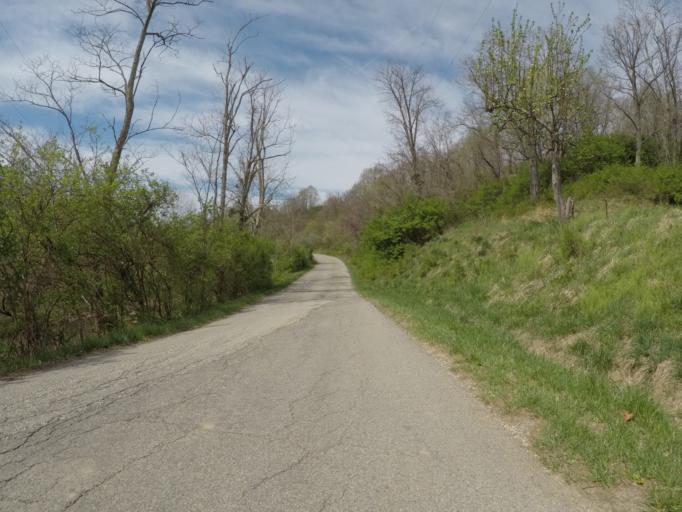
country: US
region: West Virginia
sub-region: Wayne County
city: Lavalette
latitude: 38.3448
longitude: -82.3786
